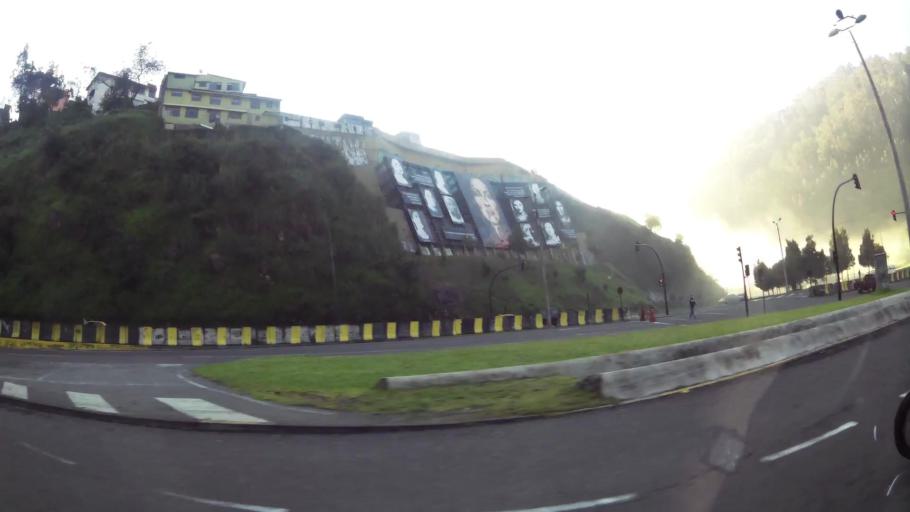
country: EC
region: Pichincha
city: Quito
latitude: -0.2313
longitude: -78.5041
